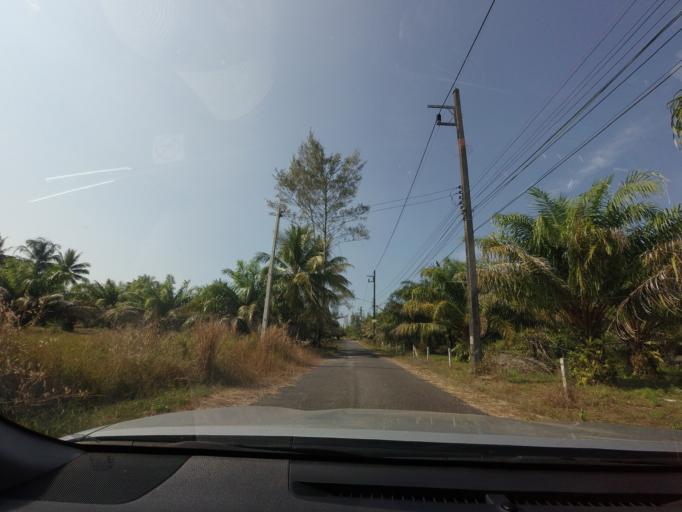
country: TH
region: Phangnga
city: Ban Khao Lak
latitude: 8.7274
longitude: 98.2426
